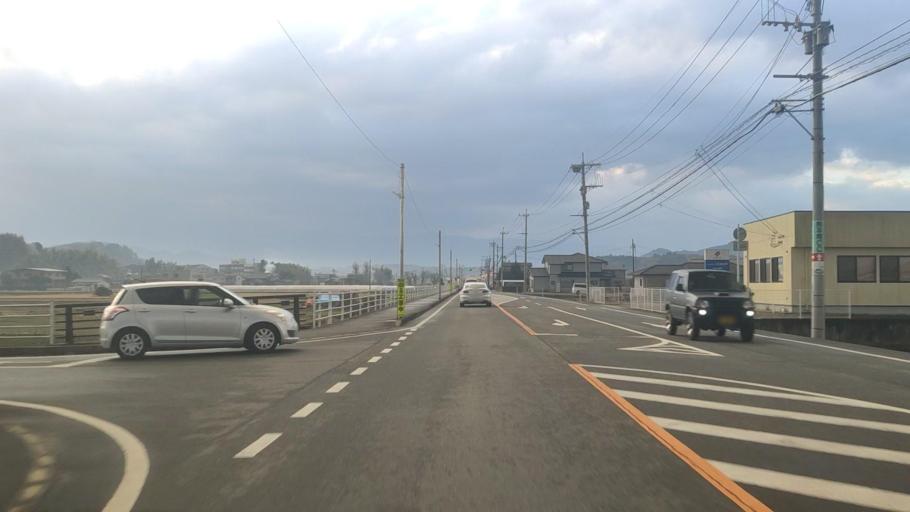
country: JP
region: Kumamoto
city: Uto
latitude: 32.7067
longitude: 130.7769
